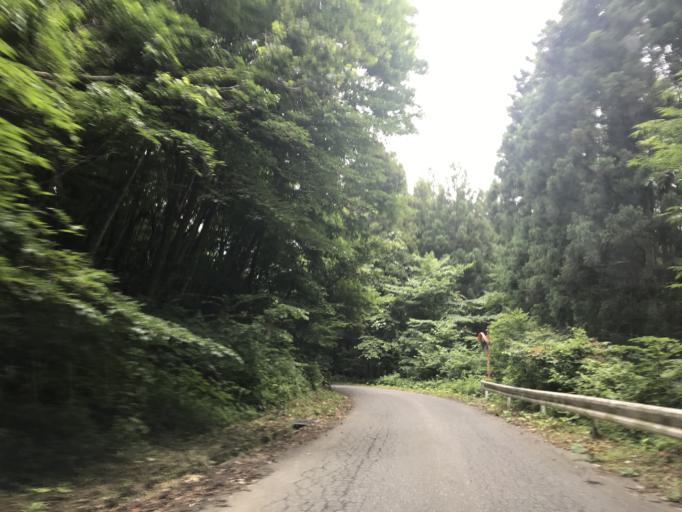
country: JP
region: Iwate
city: Ichinoseki
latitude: 38.9691
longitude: 140.9204
